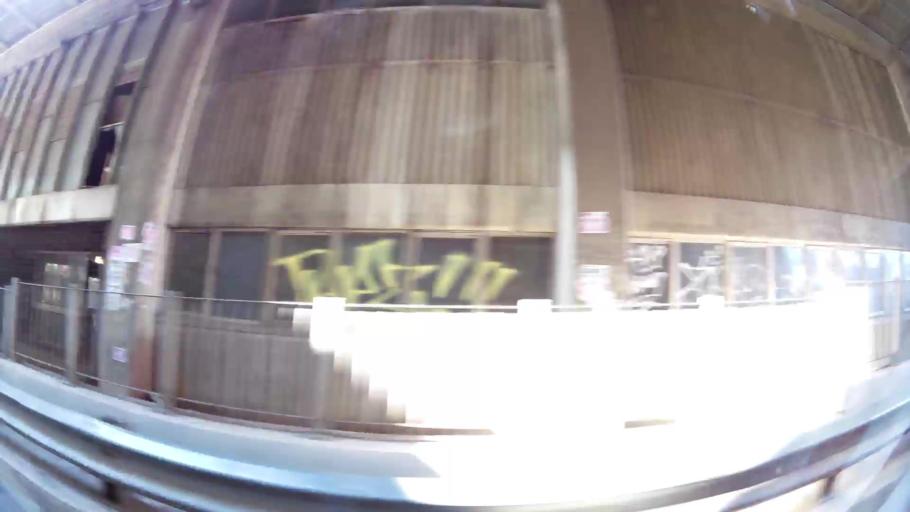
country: ZA
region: Gauteng
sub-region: City of Johannesburg Metropolitan Municipality
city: Johannesburg
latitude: -26.2052
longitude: 28.0337
